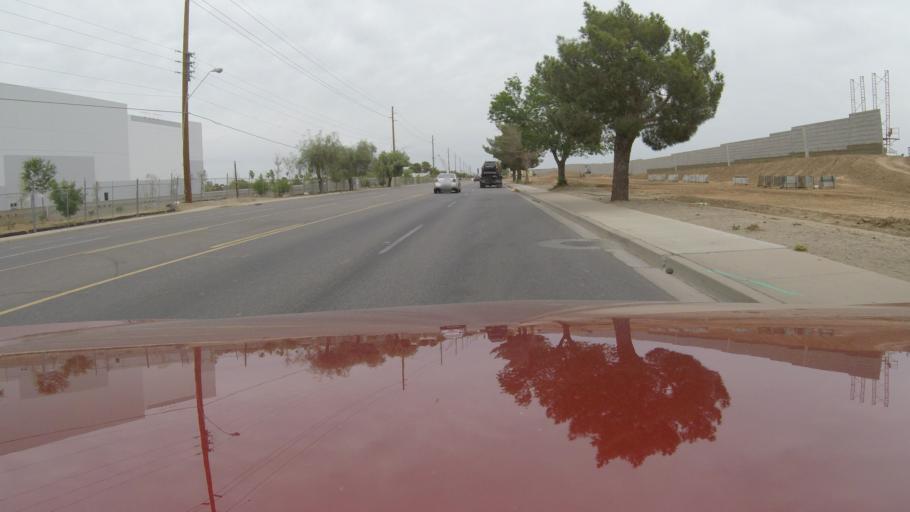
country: US
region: Arizona
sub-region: Maricopa County
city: Tolleson
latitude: 33.4530
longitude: -112.1865
